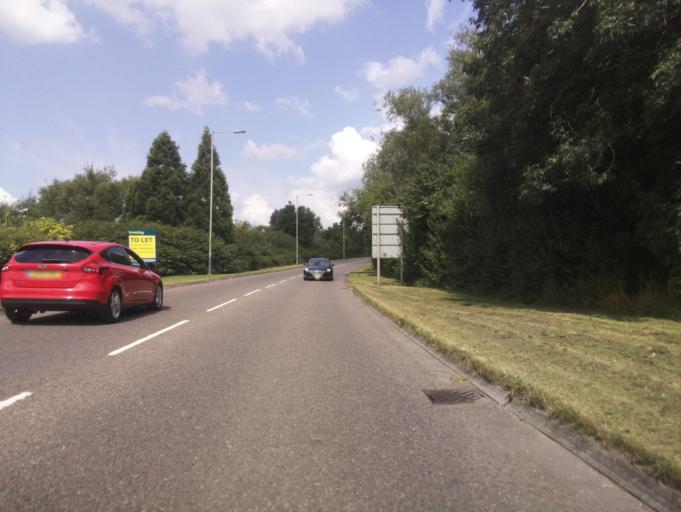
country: GB
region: England
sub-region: Wiltshire
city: Lydiard Tregoze
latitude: 51.5756
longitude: -1.8321
